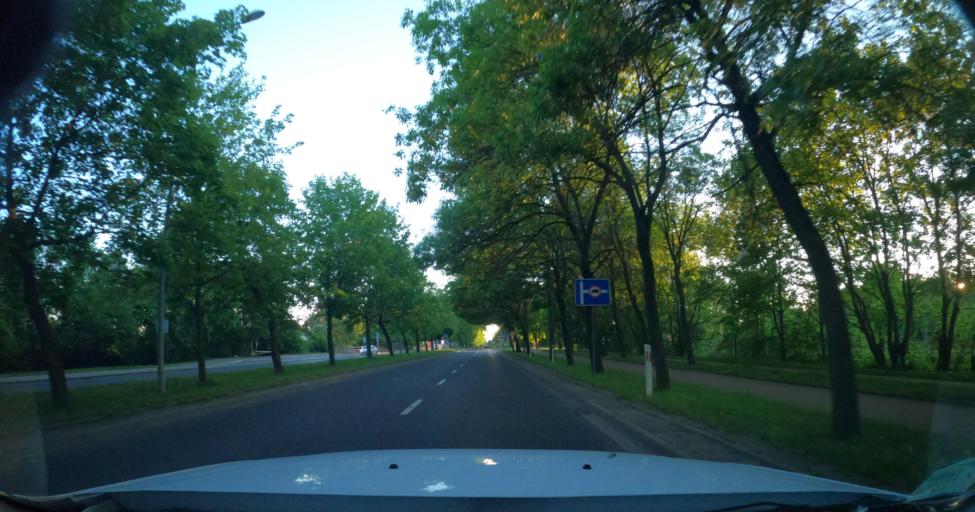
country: PL
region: Pomeranian Voivodeship
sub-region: Slupsk
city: Slupsk
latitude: 54.4682
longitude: 17.0579
